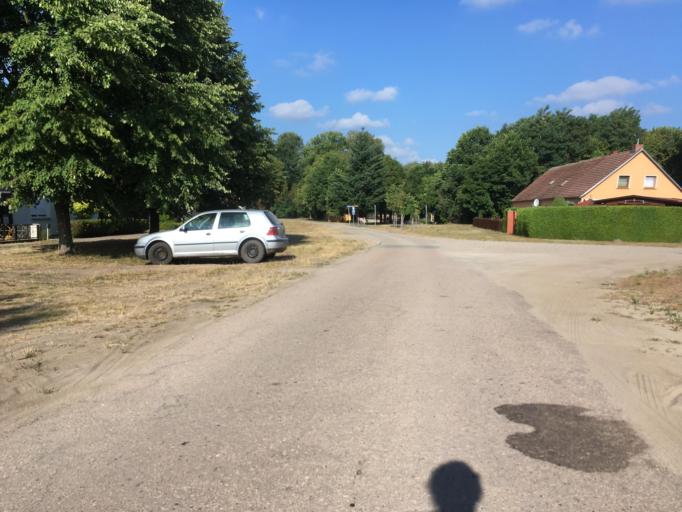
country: DE
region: Brandenburg
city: Liebenwalde
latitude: 52.9132
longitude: 13.4605
